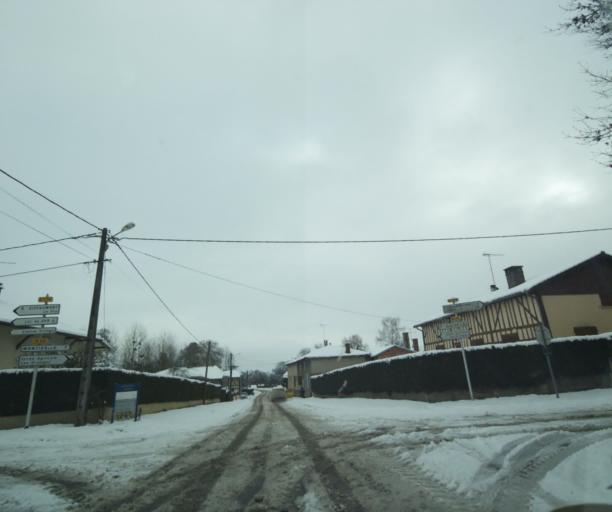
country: FR
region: Champagne-Ardenne
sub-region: Departement de la Haute-Marne
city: Montier-en-Der
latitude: 48.5117
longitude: 4.6941
